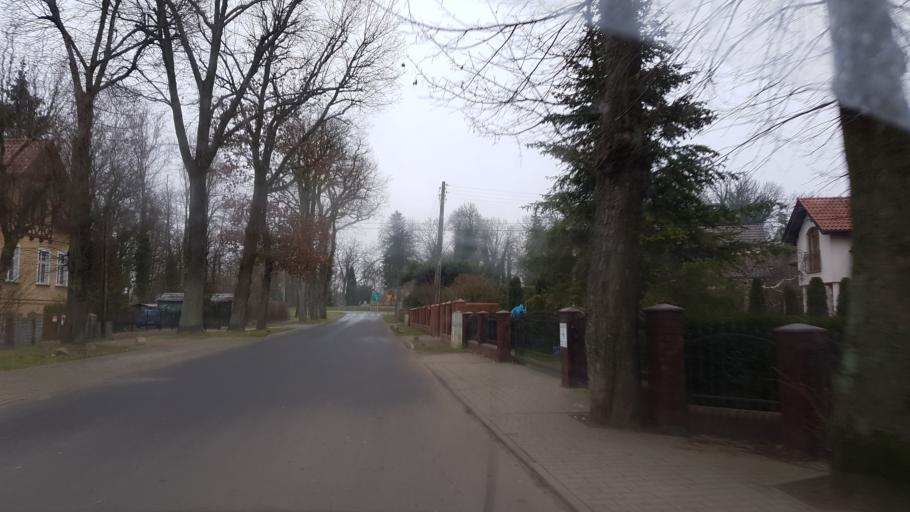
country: PL
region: West Pomeranian Voivodeship
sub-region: Powiat gryfinski
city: Chojna
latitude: 52.9638
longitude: 14.4219
